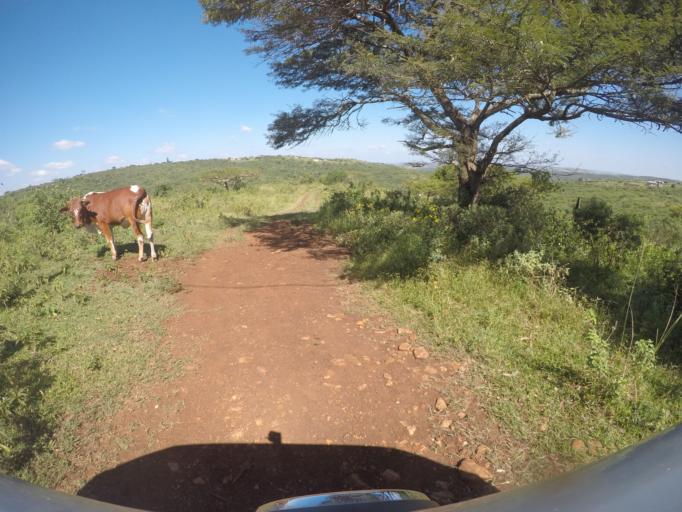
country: ZA
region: KwaZulu-Natal
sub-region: uThungulu District Municipality
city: Empangeni
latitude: -28.5651
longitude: 31.7017
